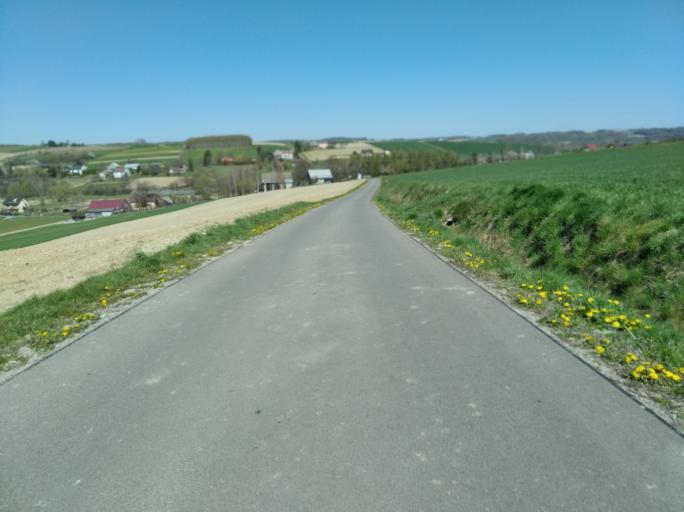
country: PL
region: Subcarpathian Voivodeship
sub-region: Powiat strzyzowski
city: Wisniowa
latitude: 49.9060
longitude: 21.6864
